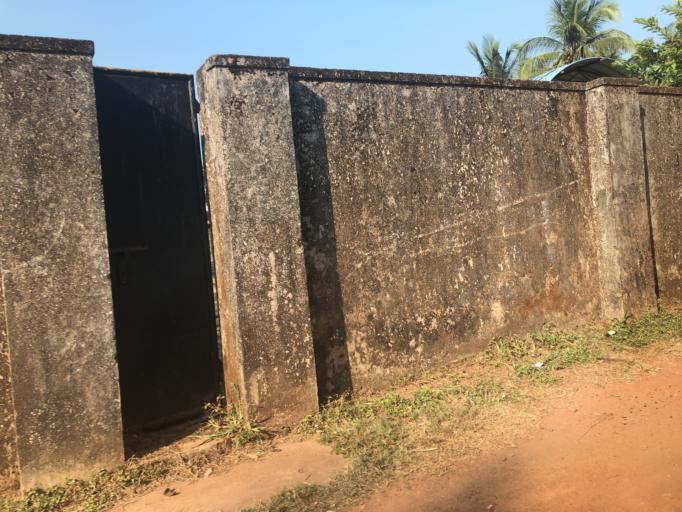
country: IN
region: Karnataka
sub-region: Dakshina Kannada
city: Ullal
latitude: 12.8211
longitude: 74.8430
